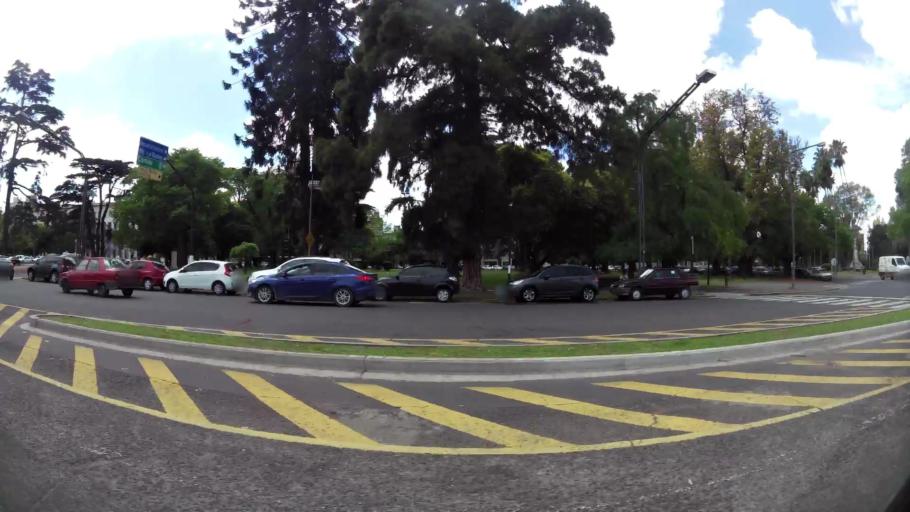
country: AR
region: Santa Fe
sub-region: Departamento de Rosario
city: Rosario
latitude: -32.9554
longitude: -60.6563
